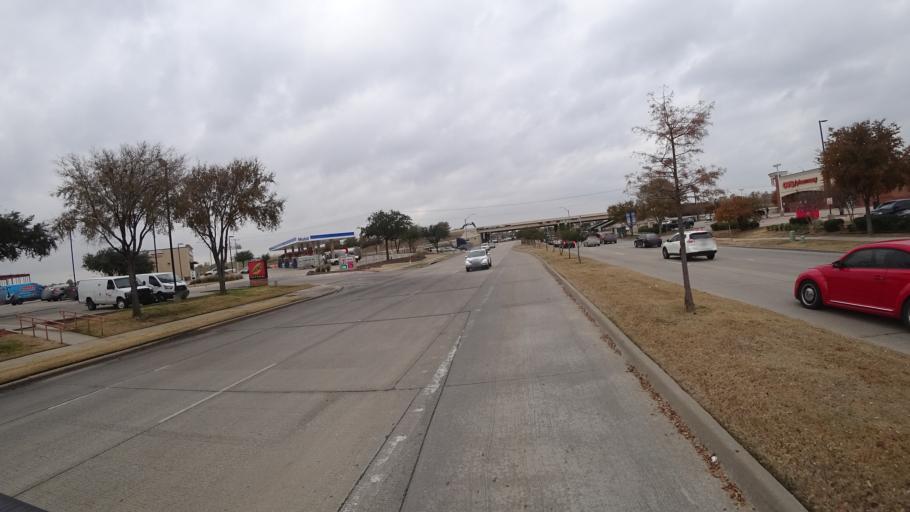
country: US
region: Texas
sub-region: Denton County
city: Lewisville
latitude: 33.0214
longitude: -96.9327
